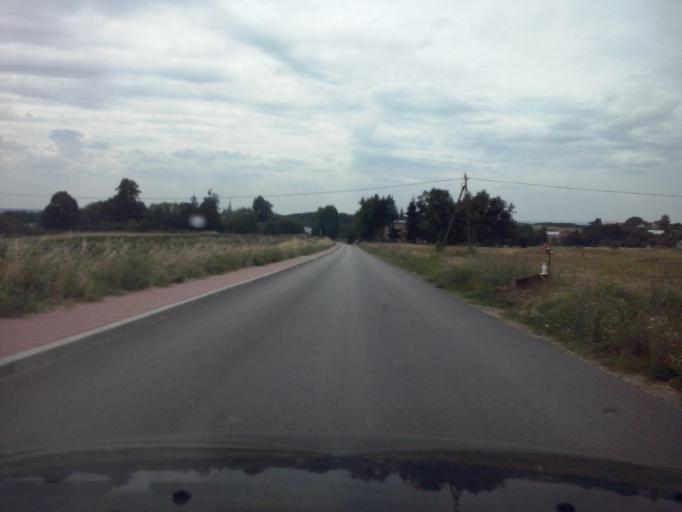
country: PL
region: Swietokrzyskie
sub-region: Powiat kielecki
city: Lagow
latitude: 50.7291
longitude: 21.1059
